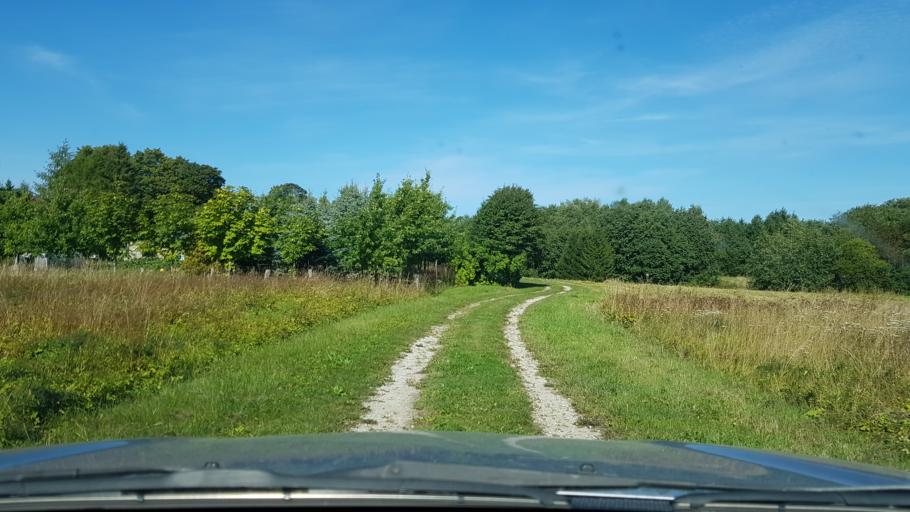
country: EE
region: Ida-Virumaa
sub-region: Sillamaee linn
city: Sillamae
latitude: 59.3912
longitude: 27.8152
